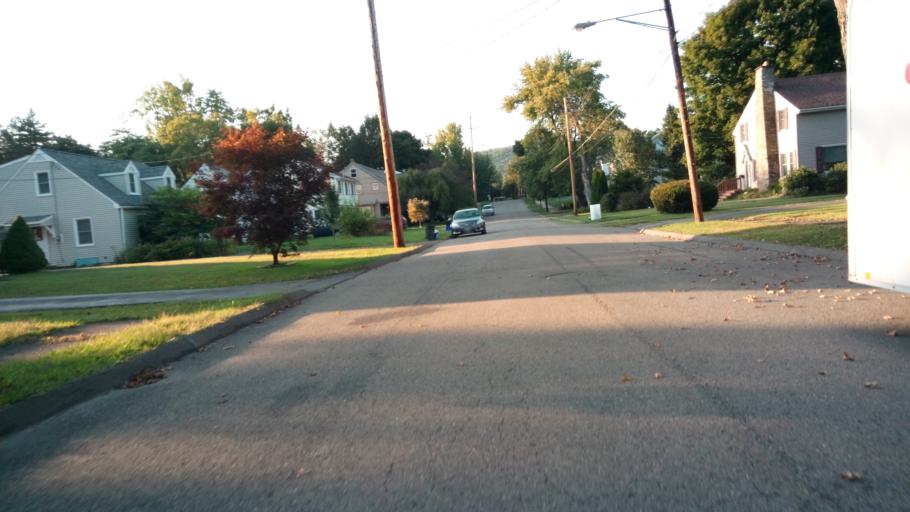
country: US
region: New York
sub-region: Chemung County
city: West Elmira
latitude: 42.0772
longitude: -76.8355
